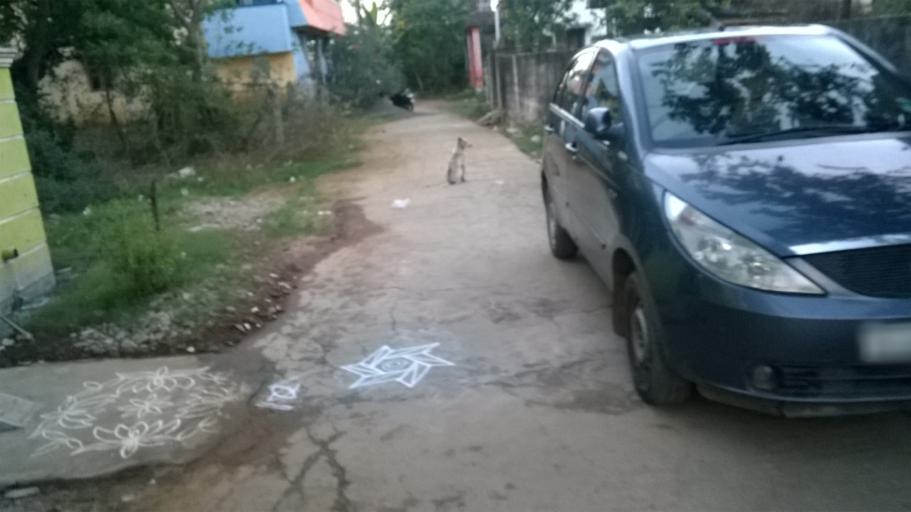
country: IN
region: Tamil Nadu
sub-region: Kancheepuram
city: Vandalur
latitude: 12.8846
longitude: 80.0781
